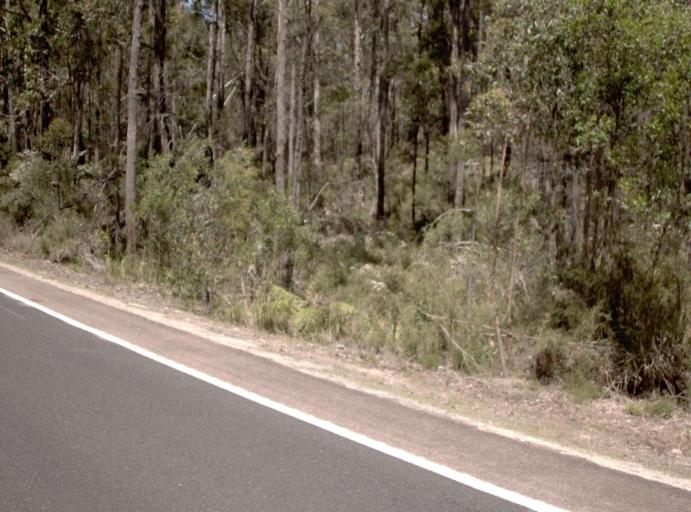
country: AU
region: New South Wales
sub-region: Bombala
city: Bombala
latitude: -37.5661
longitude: 149.1002
